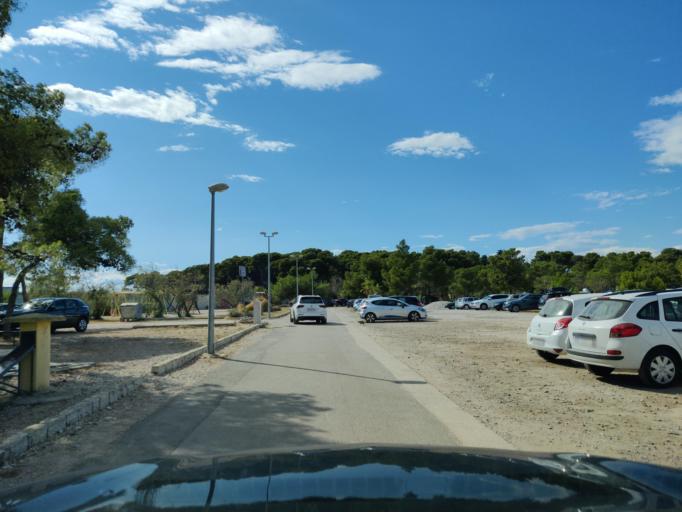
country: HR
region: Sibensko-Kniniska
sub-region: Grad Sibenik
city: Sibenik
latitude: 43.7234
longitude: 15.8478
